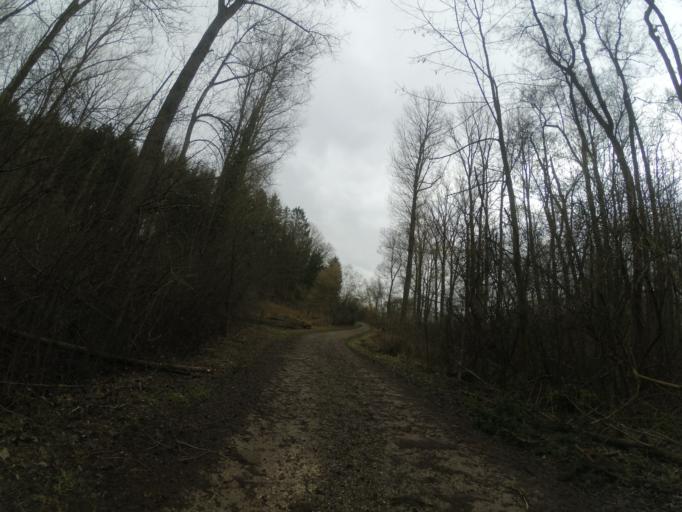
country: DE
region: Bavaria
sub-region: Swabia
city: Vohringen
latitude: 48.2937
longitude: 10.0955
